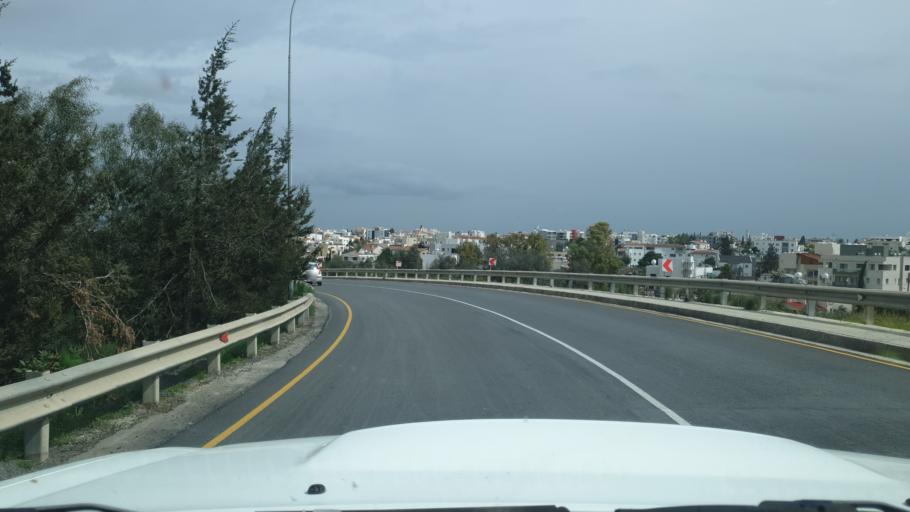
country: CY
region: Lefkosia
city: Geri
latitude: 35.1037
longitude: 33.3701
